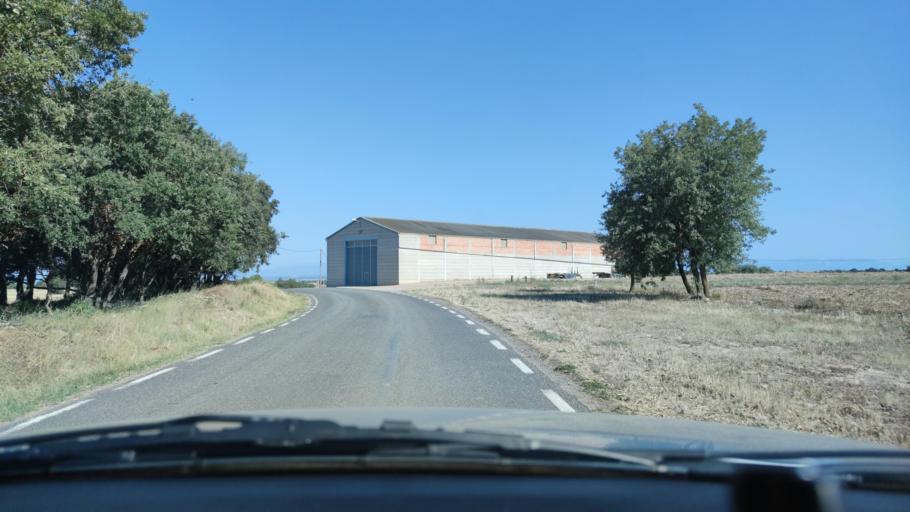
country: ES
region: Catalonia
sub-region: Provincia de Lleida
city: Ivorra
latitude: 41.7307
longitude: 1.3645
